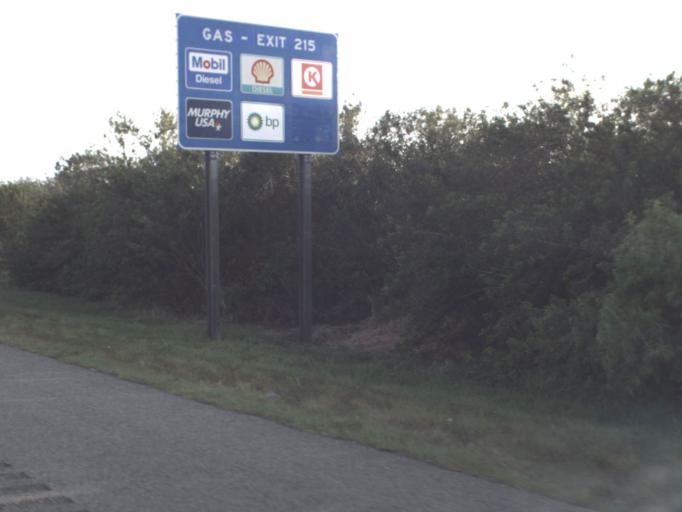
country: US
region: Florida
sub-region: Brevard County
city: Titusville
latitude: 28.5585
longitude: -80.8517
